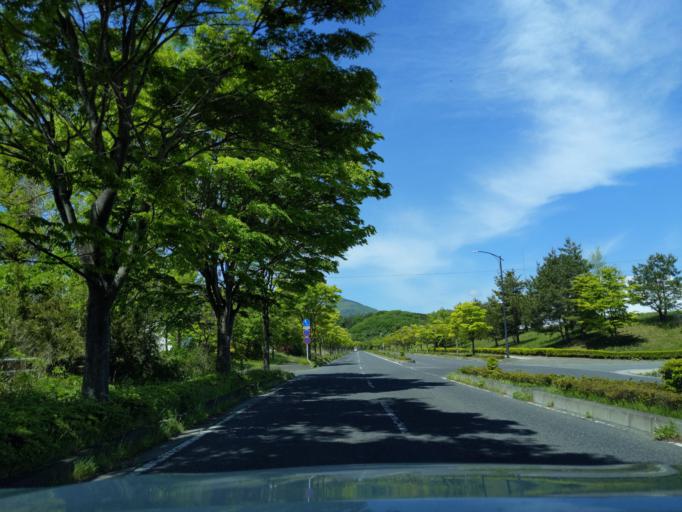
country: JP
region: Fukushima
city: Koriyama
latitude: 37.4471
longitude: 140.2962
